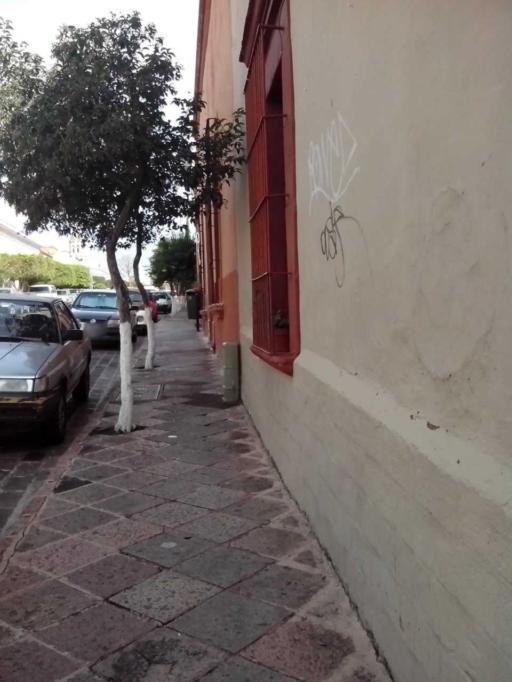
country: MX
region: Queretaro
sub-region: Queretaro
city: Santiago de Queretaro
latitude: 20.5932
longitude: -100.3866
